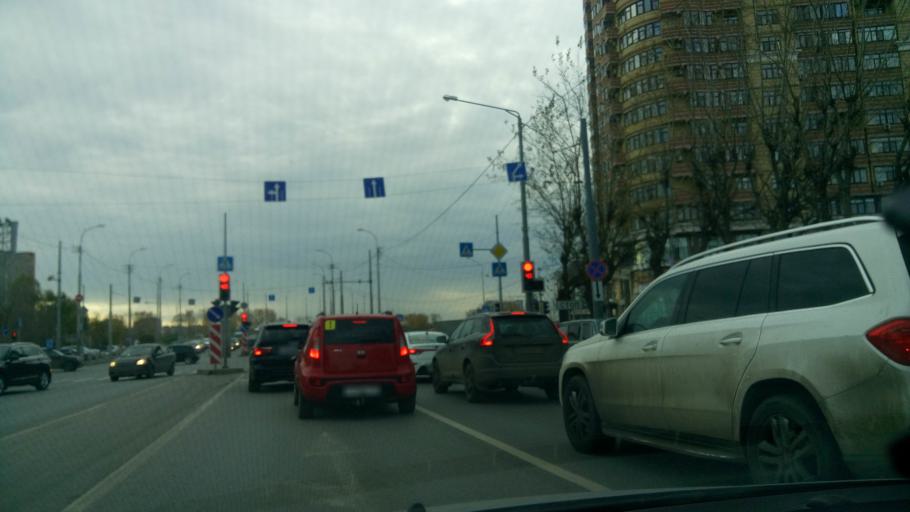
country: RU
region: Tjumen
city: Tyumen
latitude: 57.1351
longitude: 65.5655
